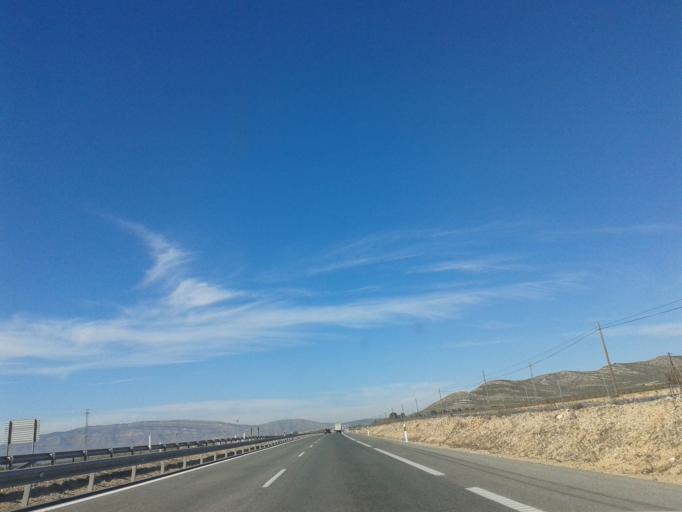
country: ES
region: Valencia
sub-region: Provincia de Alicante
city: Villena
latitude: 38.6820
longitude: -0.8996
